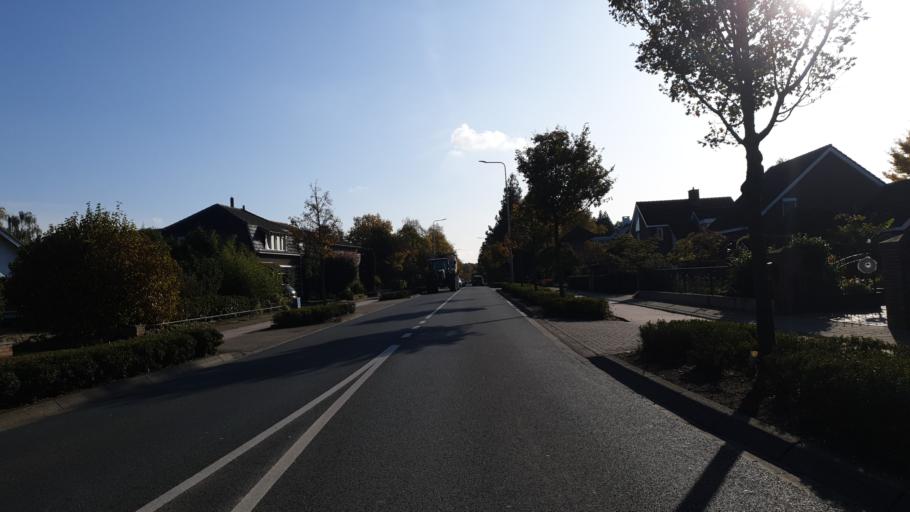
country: NL
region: Limburg
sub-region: Gemeente Venlo
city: Venlo
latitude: 51.4125
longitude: 6.1657
